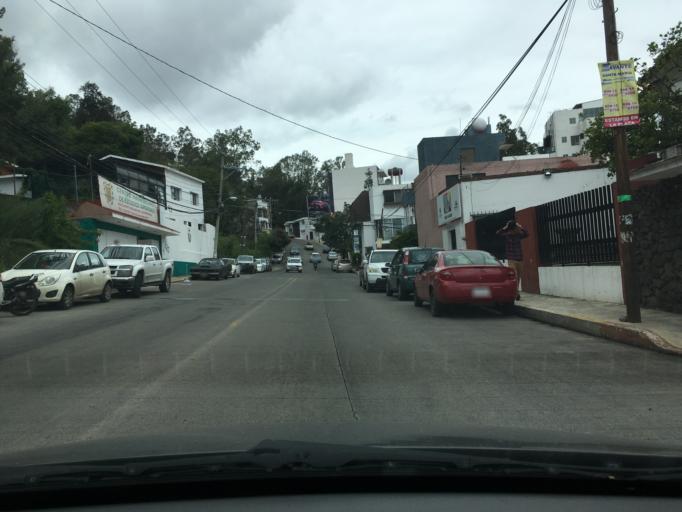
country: MX
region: Michoacan
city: Morelia
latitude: 19.6797
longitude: -101.1831
